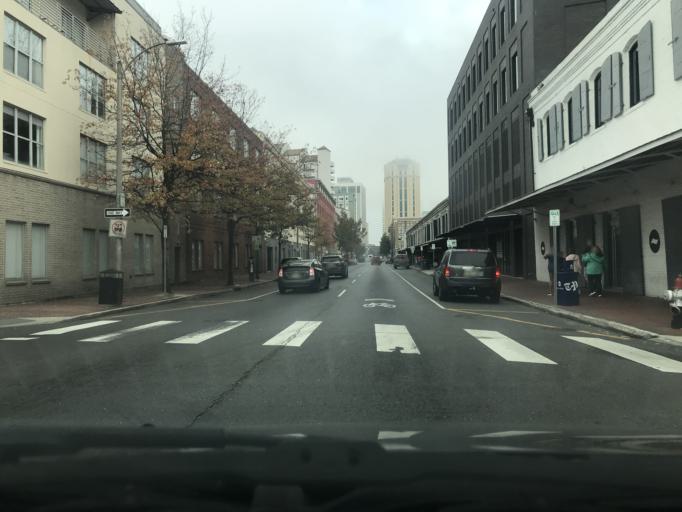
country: US
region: Louisiana
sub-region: Orleans Parish
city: New Orleans
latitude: 29.9429
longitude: -90.0658
